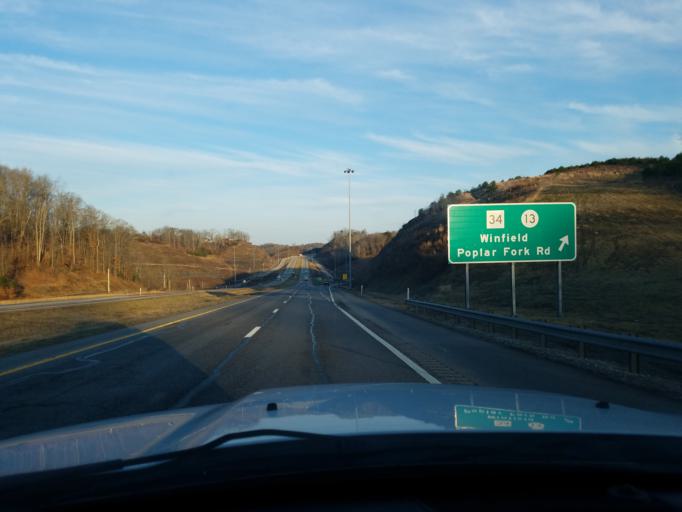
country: US
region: West Virginia
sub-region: Putnam County
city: Teays Valley
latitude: 38.4787
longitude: -81.9223
